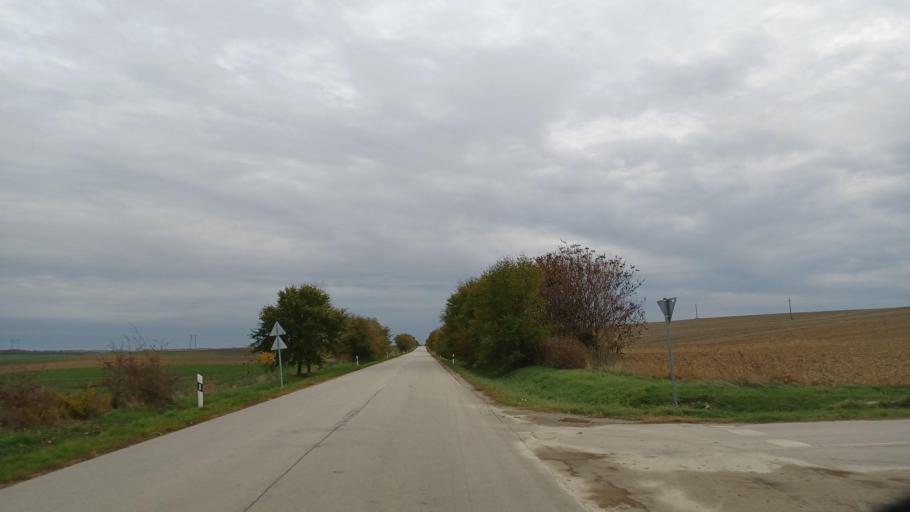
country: HU
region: Tolna
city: Nagydorog
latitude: 46.6798
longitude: 18.5997
